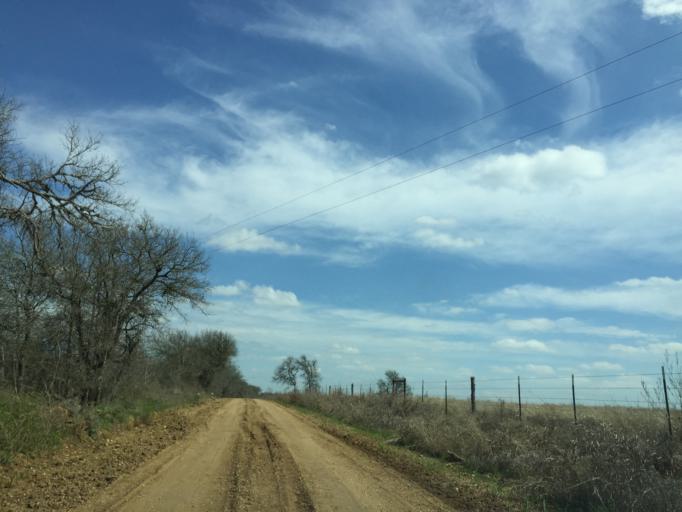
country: US
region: Texas
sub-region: Milam County
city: Thorndale
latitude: 30.5597
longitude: -97.1912
